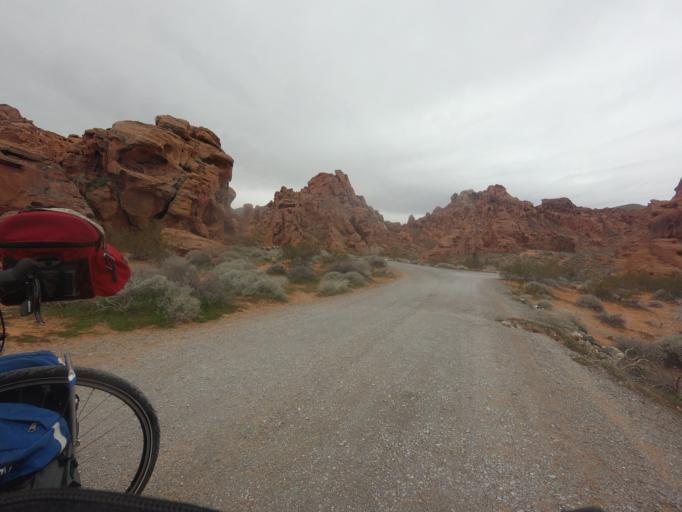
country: US
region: Nevada
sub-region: Clark County
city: Moapa Valley
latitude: 36.4164
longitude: -114.5532
